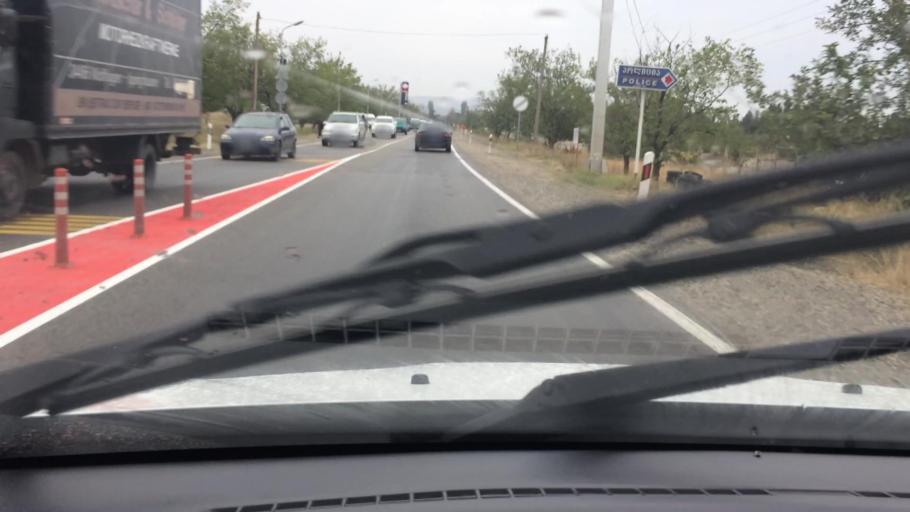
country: GE
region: Kvemo Kartli
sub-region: Marneuli
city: Marneuli
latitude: 41.5723
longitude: 44.7750
